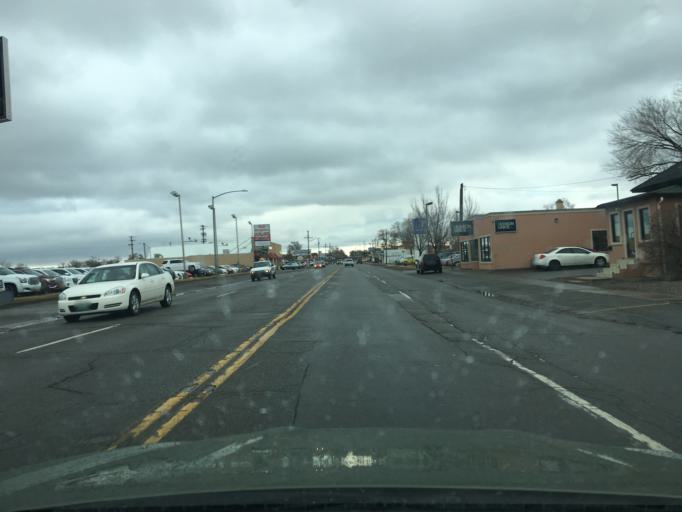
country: US
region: Colorado
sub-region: Mesa County
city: Grand Junction
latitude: 39.0735
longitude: -108.5708
